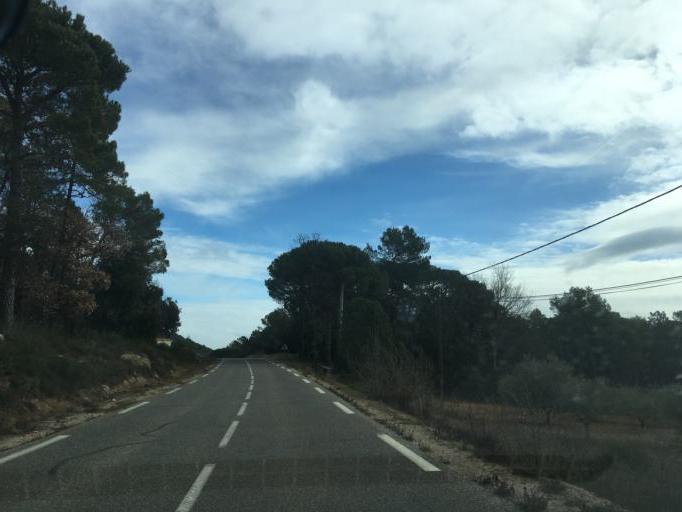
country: FR
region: Provence-Alpes-Cote d'Azur
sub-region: Departement du Var
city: Le Val
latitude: 43.4436
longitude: 6.0251
